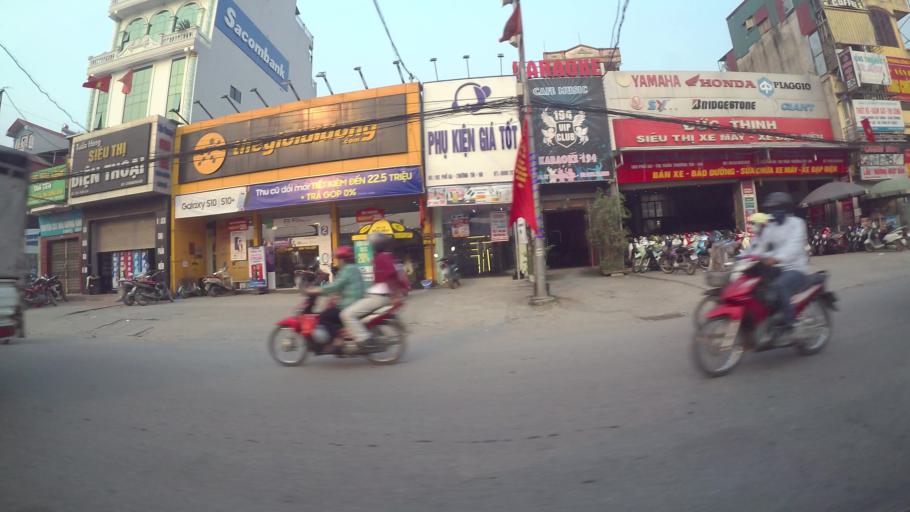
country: VN
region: Ha Noi
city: Thuong Tin
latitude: 20.8719
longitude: 105.8644
